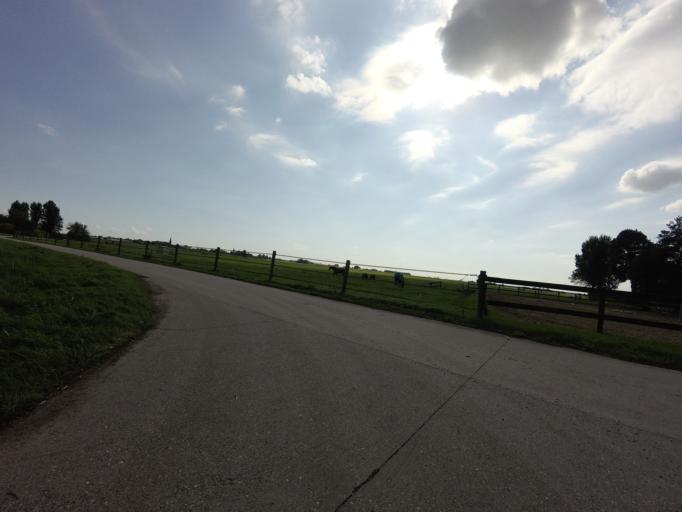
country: NL
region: Friesland
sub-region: Gemeente Littenseradiel
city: Makkum
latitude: 53.0857
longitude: 5.6314
